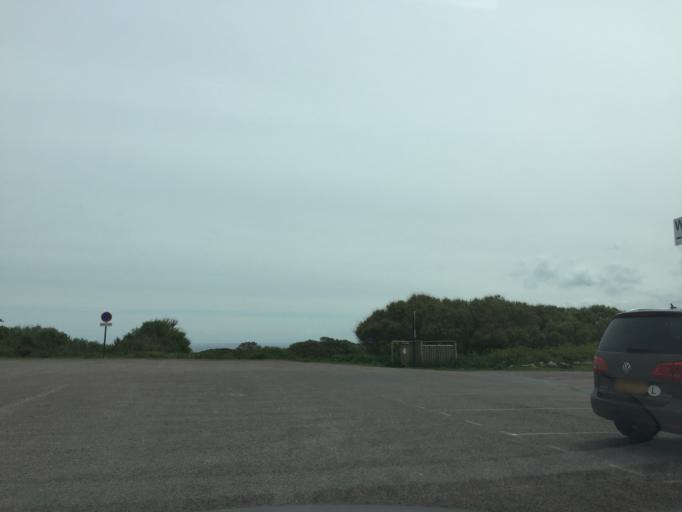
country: FR
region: Brittany
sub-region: Departement des Cotes-d'Armor
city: Saint-Cast-le-Guildo
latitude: 48.6833
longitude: -2.3190
